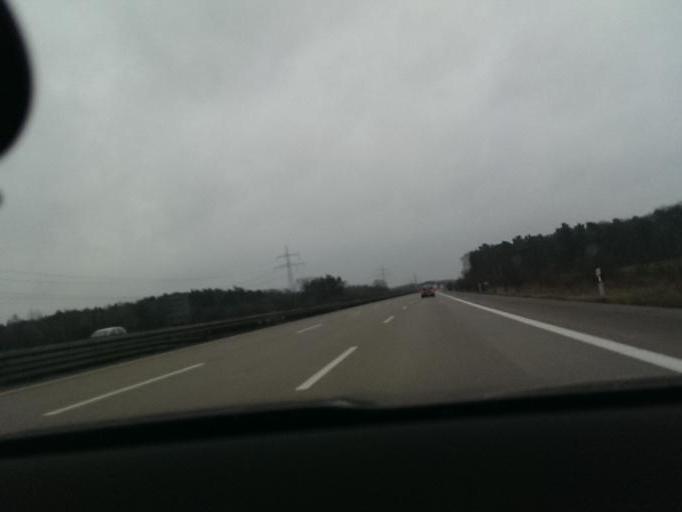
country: DE
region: Lower Saxony
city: Isernhagen Farster Bauerschaft
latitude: 52.5329
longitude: 9.8076
